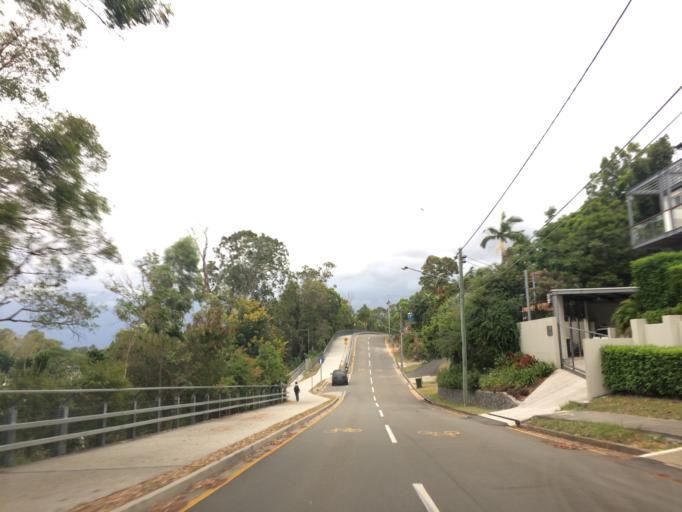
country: AU
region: Queensland
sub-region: Brisbane
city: Yeronga
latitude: -27.5046
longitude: 153.0037
